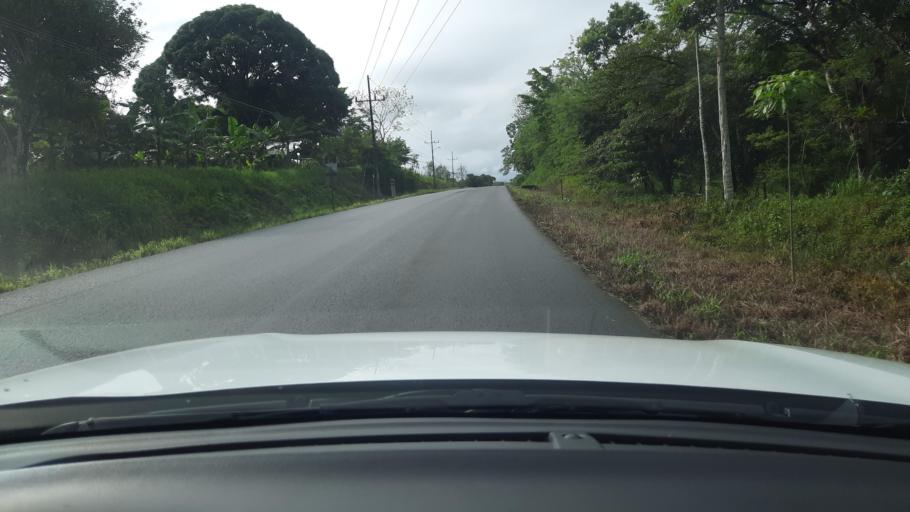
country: CR
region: Alajuela
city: San Jose
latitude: 10.9440
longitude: -85.1163
